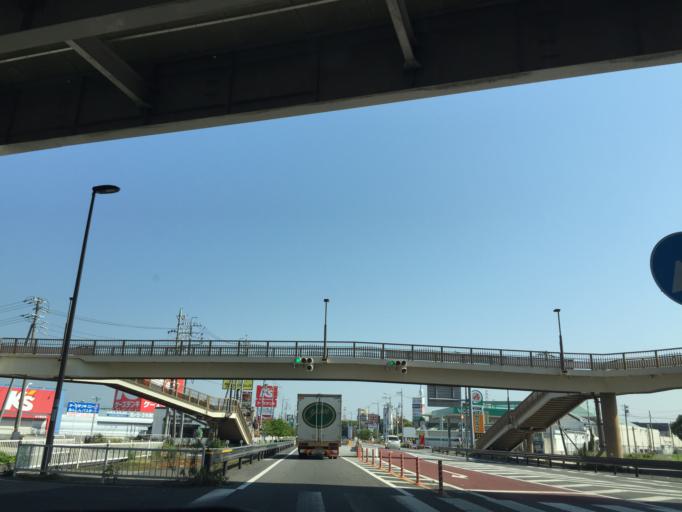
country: JP
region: Mie
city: Yokkaichi
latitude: 35.0287
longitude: 136.6717
